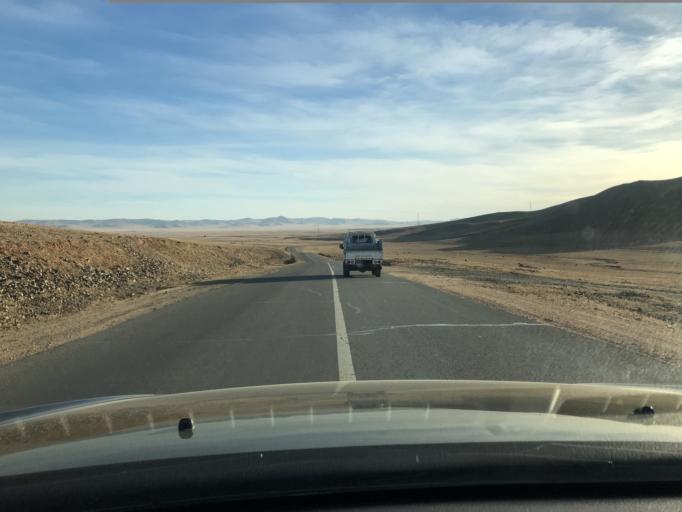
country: MN
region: Central Aimak
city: Dzuunmod
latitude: 47.8053
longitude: 107.3237
